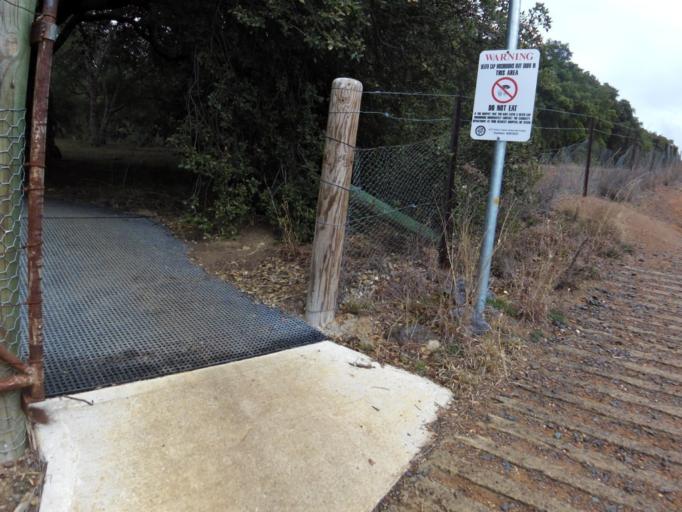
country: AU
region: Australian Capital Territory
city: Macquarie
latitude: -35.2791
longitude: 149.0809
